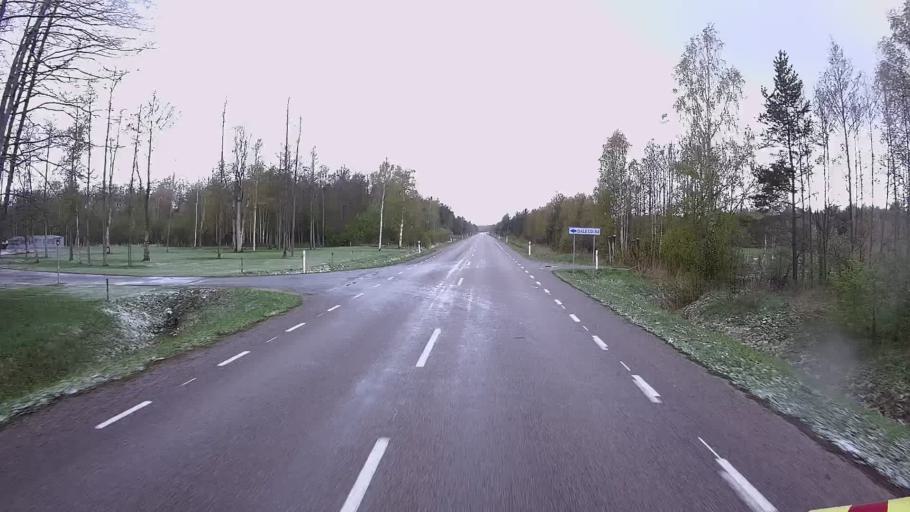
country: EE
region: Hiiumaa
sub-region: Kaerdla linn
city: Kardla
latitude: 58.7782
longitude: 22.5046
